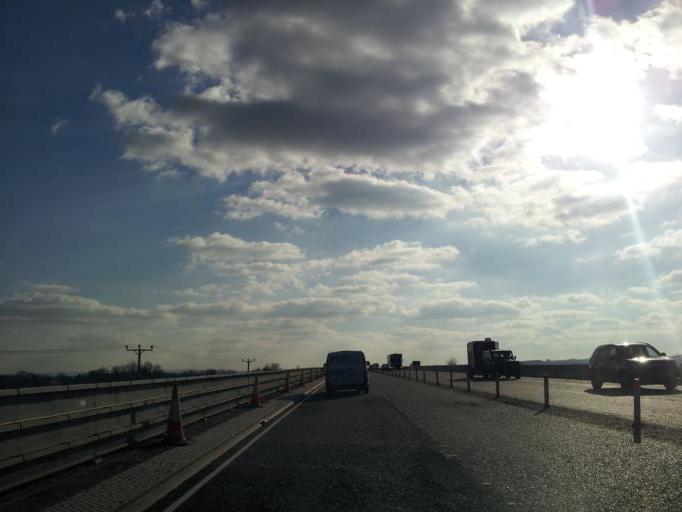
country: GB
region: England
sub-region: Somerset
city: Bridgwater
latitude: 51.1155
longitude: -2.9785
